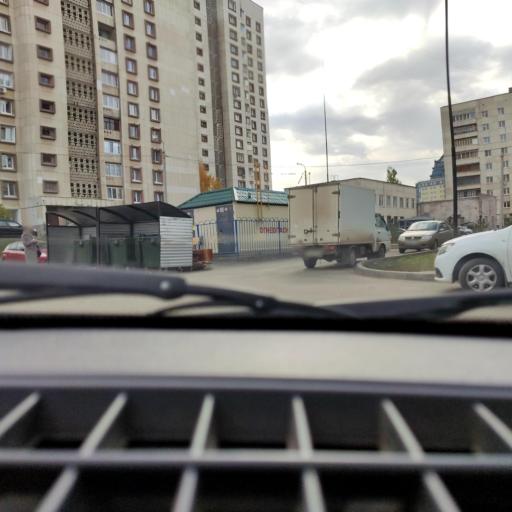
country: RU
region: Bashkortostan
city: Ufa
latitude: 54.7122
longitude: 55.9727
